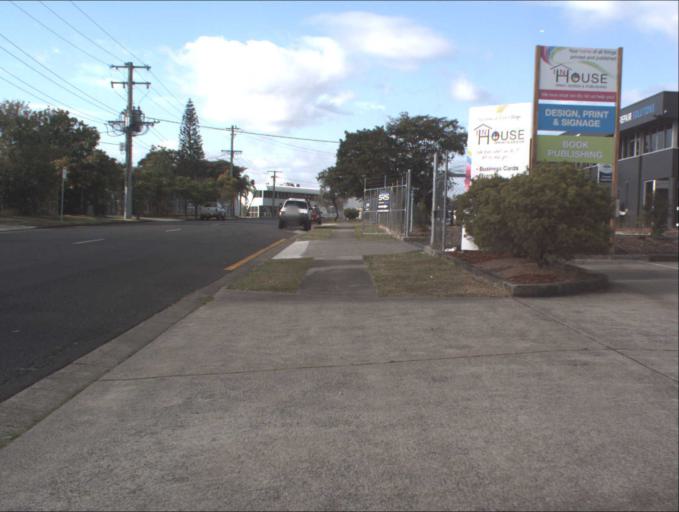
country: AU
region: Queensland
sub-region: Logan
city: Springwood
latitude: -27.6184
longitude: 153.1185
